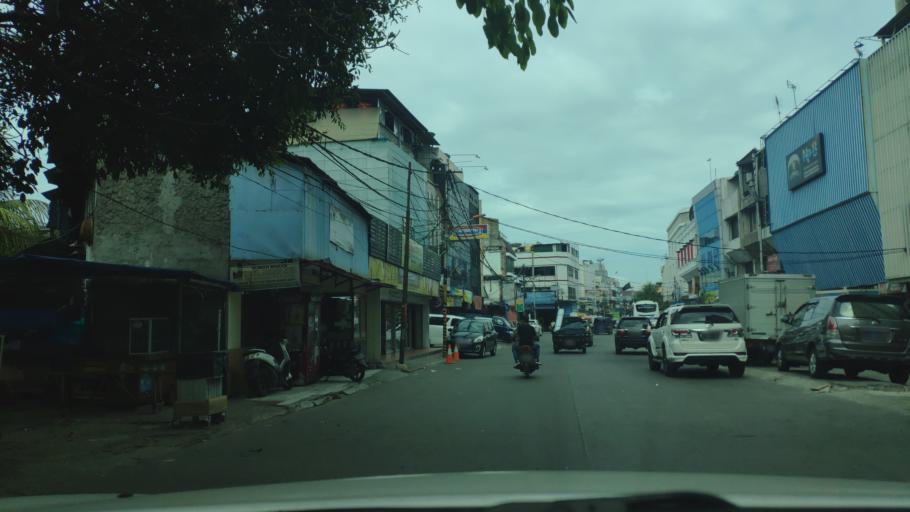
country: ID
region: Jakarta Raya
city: Jakarta
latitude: -6.1471
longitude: 106.8175
